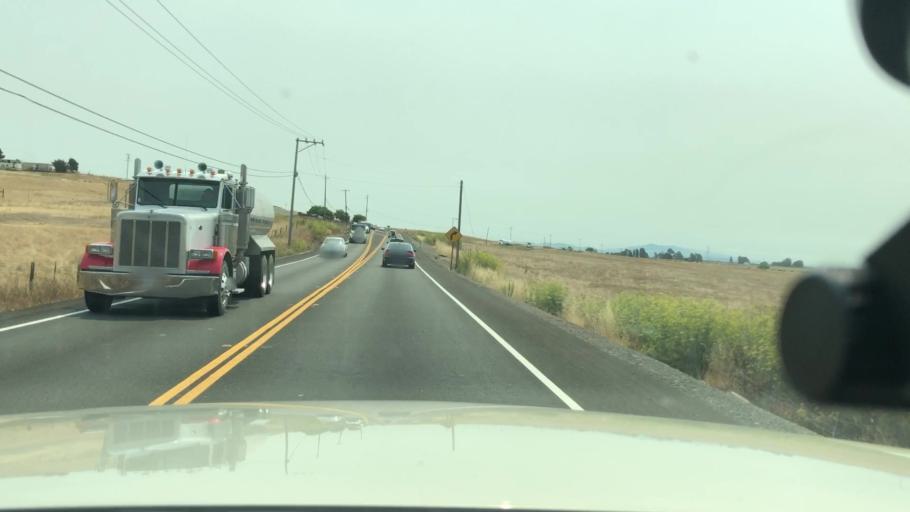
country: US
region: California
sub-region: Marin County
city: Black Point-Green Point
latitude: 38.1532
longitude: -122.4925
